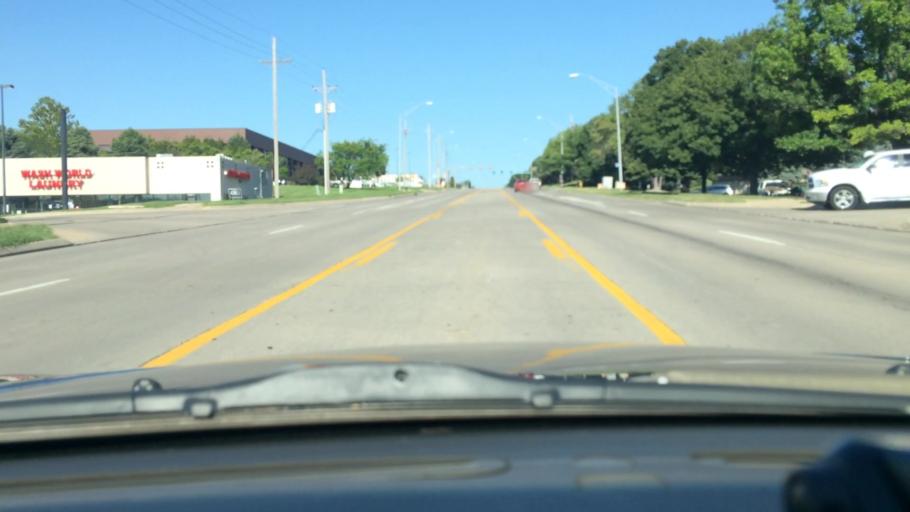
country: US
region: Nebraska
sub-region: Douglas County
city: Ralston
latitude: 41.2054
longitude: -96.0645
